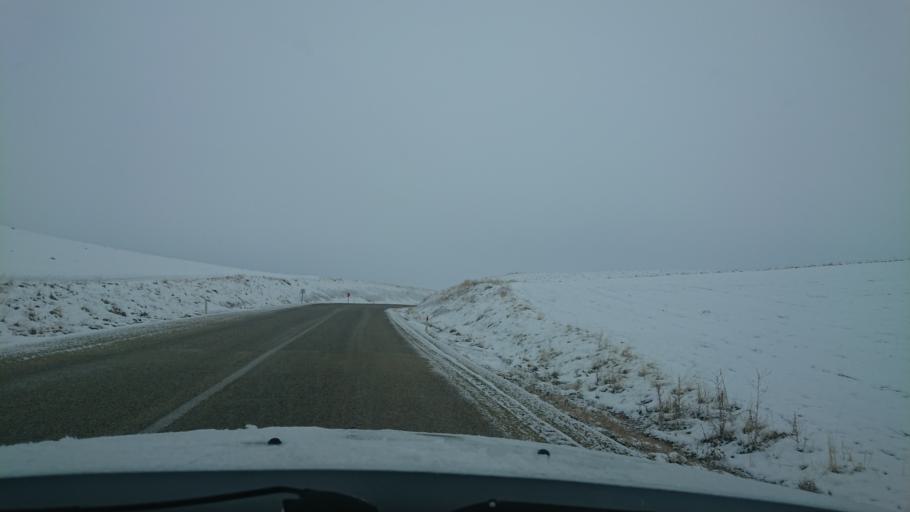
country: TR
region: Aksaray
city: Agacoren
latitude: 38.7703
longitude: 33.8694
